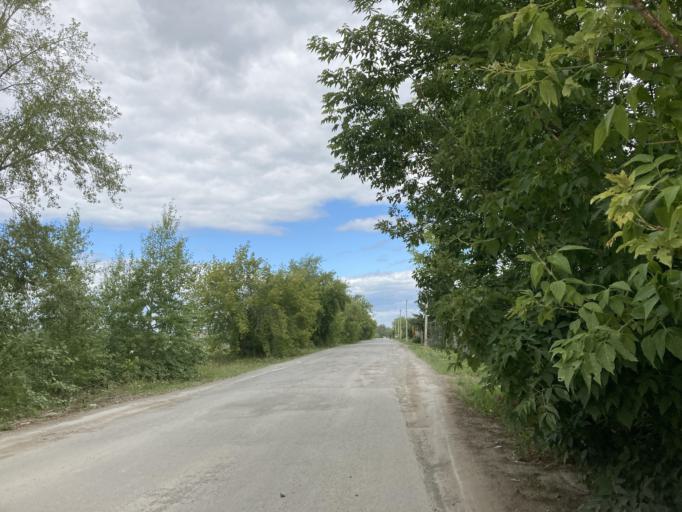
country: RU
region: Sverdlovsk
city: Bogdanovich
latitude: 56.7893
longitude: 62.0669
